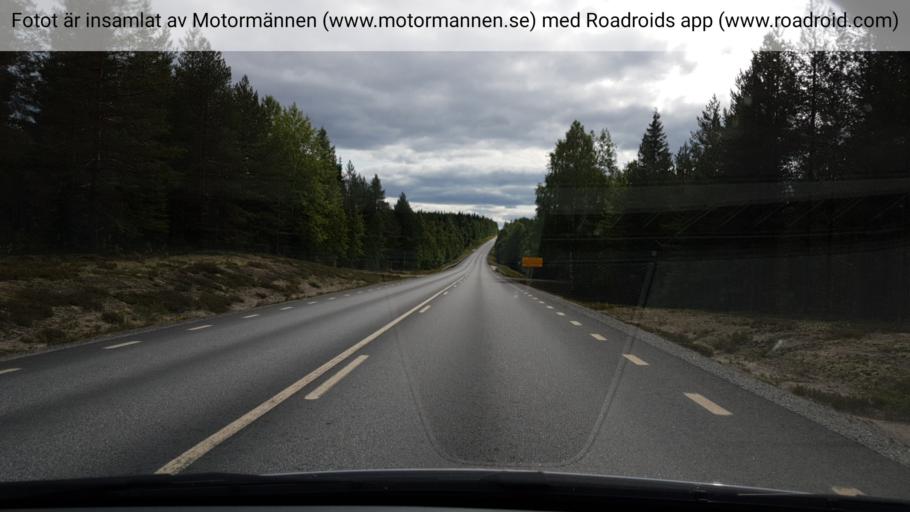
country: SE
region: Vaesterbotten
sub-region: Vannas Kommun
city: Vannasby
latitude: 64.0613
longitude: 19.9945
